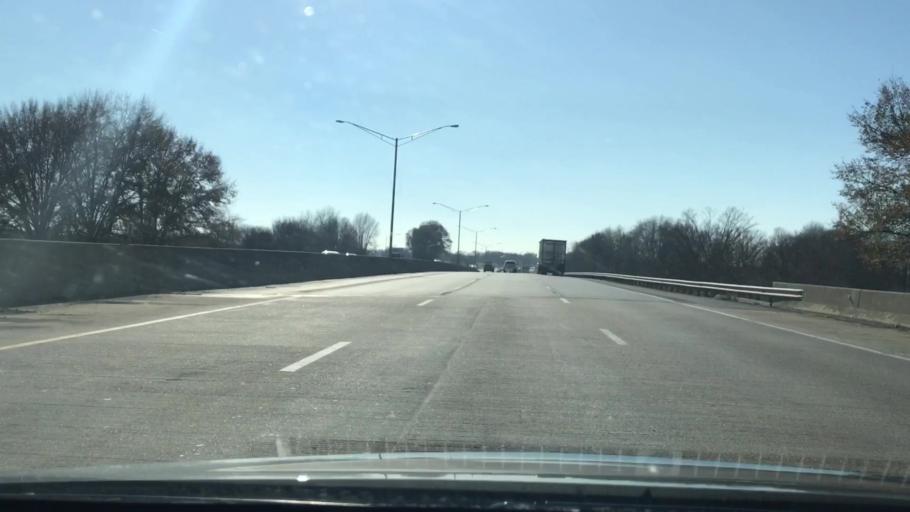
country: US
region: Kentucky
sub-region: Edmonson County
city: Brownsville
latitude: 37.0298
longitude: -86.2397
